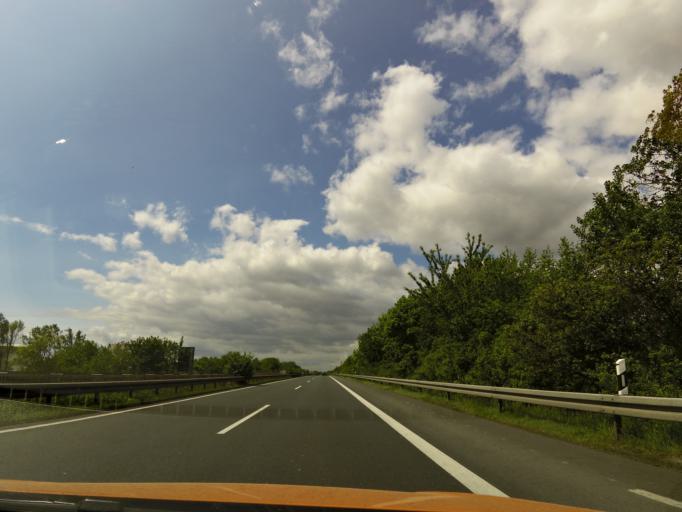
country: DE
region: Lower Saxony
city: Leiferde
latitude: 52.1963
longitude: 10.4266
